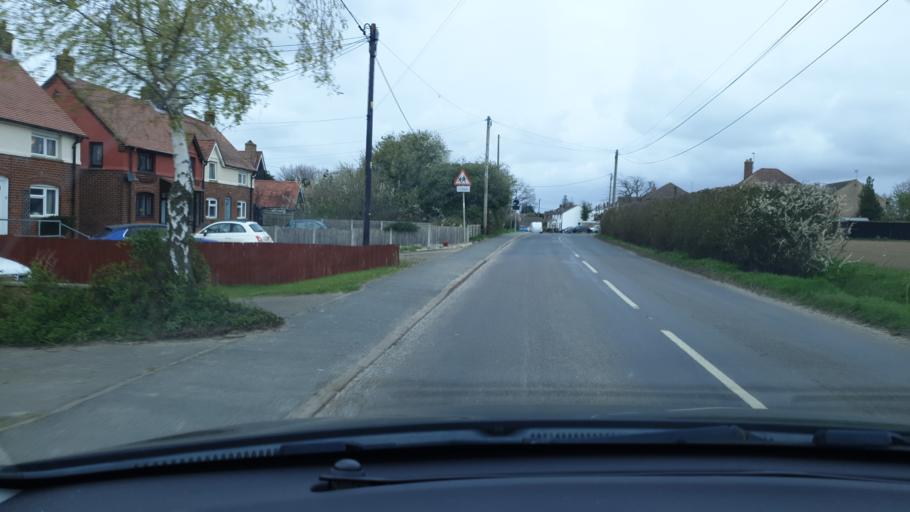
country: GB
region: England
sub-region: Essex
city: Mistley
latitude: 51.9107
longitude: 1.1363
